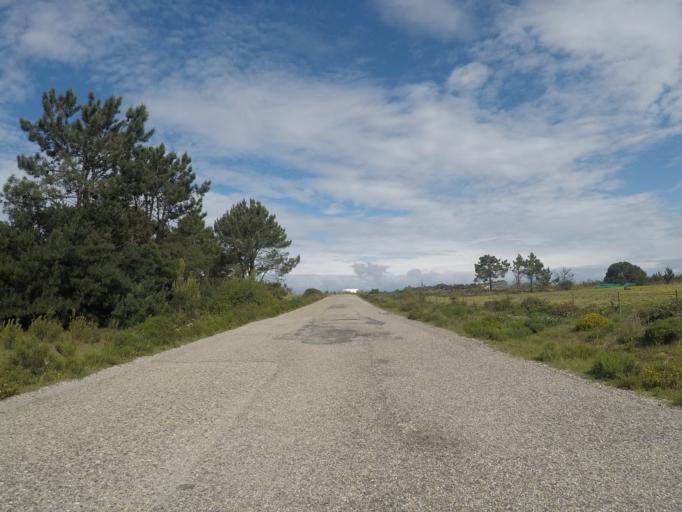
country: PT
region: Beja
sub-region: Odemira
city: Sao Teotonio
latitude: 37.4486
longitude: -8.7647
